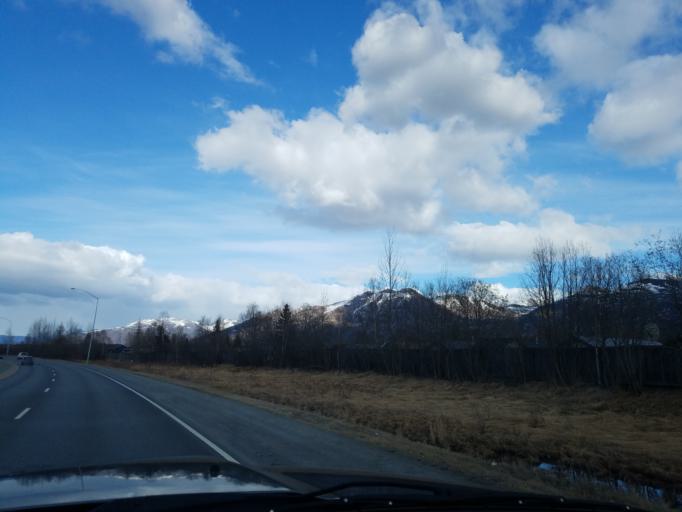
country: US
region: Alaska
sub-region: Anchorage Municipality
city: Elmendorf Air Force Base
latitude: 61.1824
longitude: -149.7373
